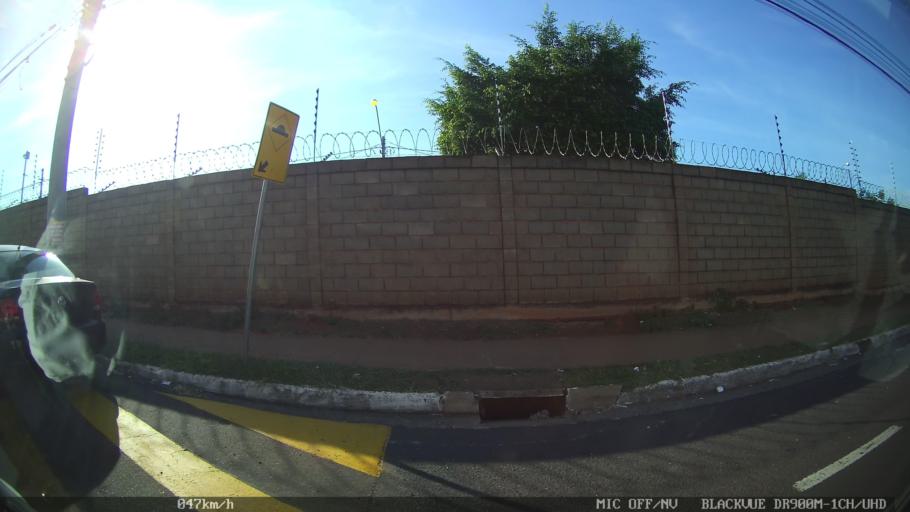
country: BR
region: Sao Paulo
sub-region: Sao Jose Do Rio Preto
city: Sao Jose do Rio Preto
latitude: -20.7796
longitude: -49.3424
